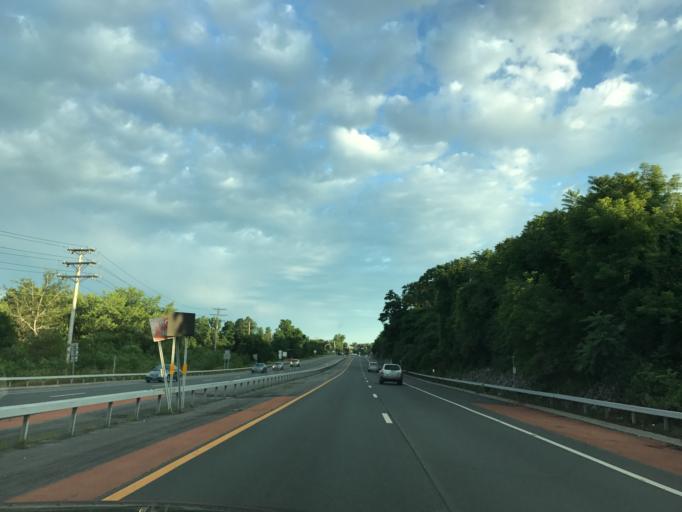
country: US
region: New York
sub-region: Albany County
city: Cohoes
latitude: 42.7731
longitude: -73.6970
